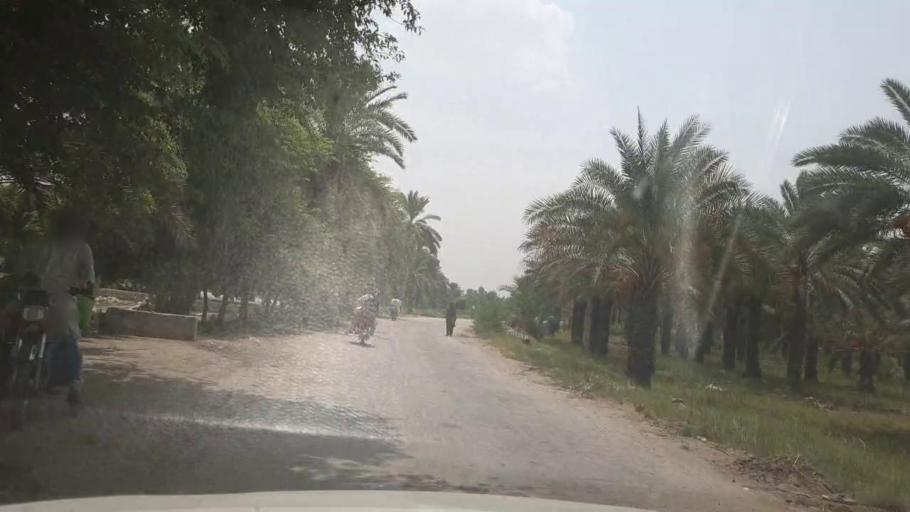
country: PK
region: Sindh
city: Kot Diji
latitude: 27.3726
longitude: 68.7201
